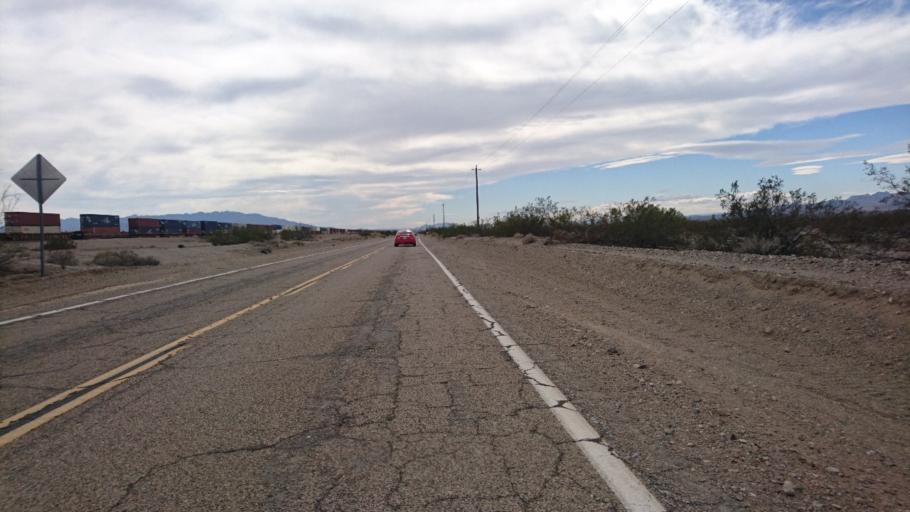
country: US
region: California
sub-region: San Bernardino County
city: Needles
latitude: 34.7975
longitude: -115.1974
